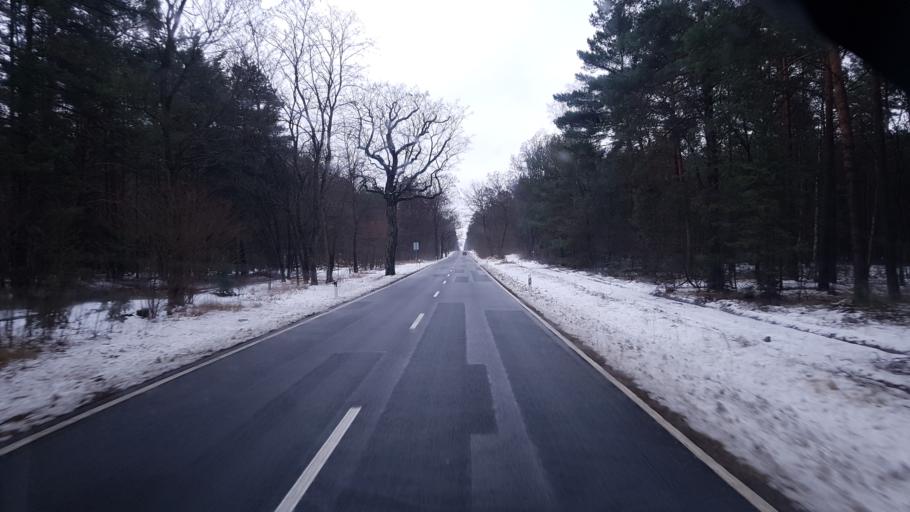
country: DE
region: Brandenburg
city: Jamlitz
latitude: 51.9831
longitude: 14.4373
